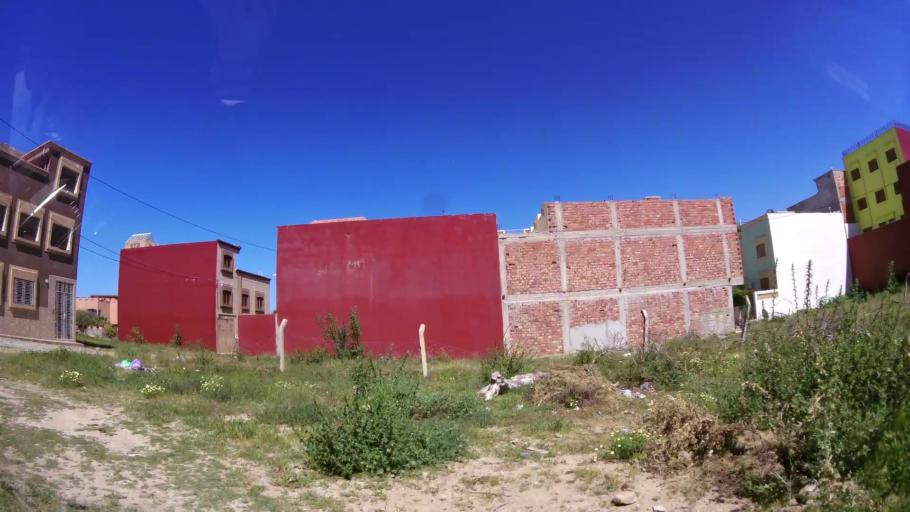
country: MA
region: Oriental
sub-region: Berkane-Taourirt
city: Madagh
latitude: 35.1373
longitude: -2.4263
